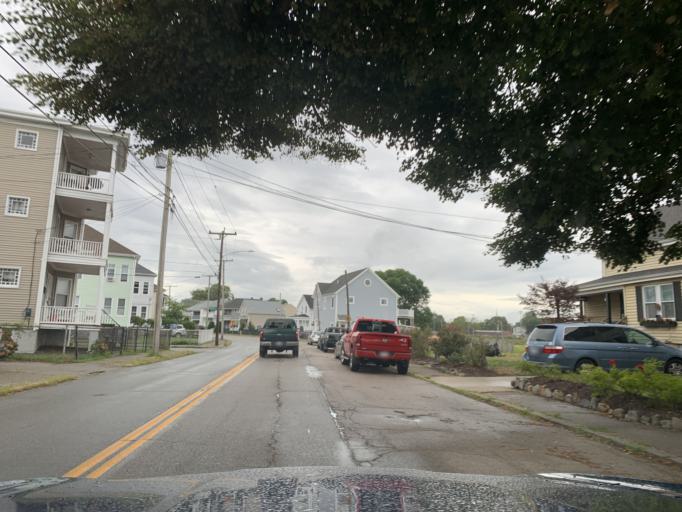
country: US
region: Rhode Island
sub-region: Bristol County
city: Warren
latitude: 41.7329
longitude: -71.2741
